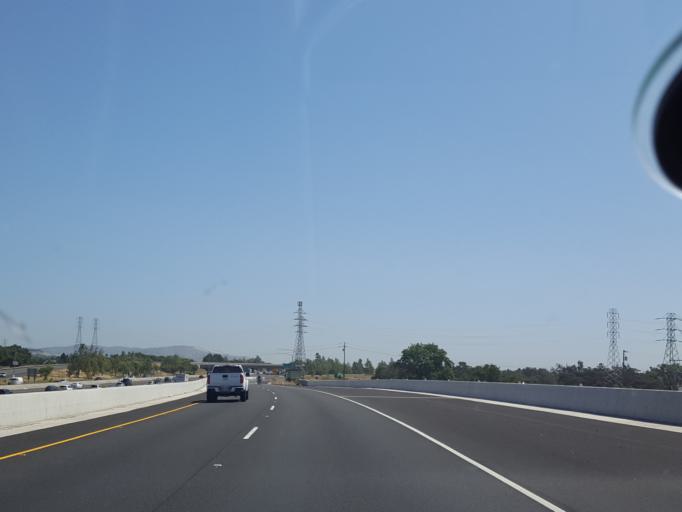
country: US
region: California
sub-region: Solano County
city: Suisun
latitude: 38.2363
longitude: -122.0991
